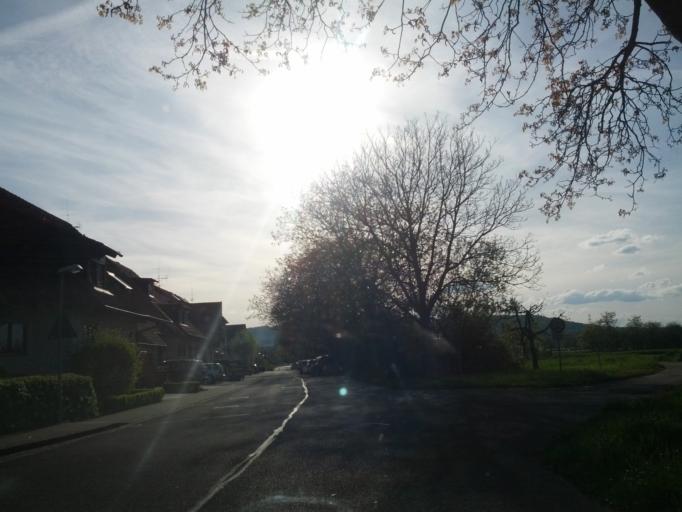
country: DE
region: Baden-Wuerttemberg
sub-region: Freiburg Region
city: Eichstetten
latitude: 48.1064
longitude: 7.7715
